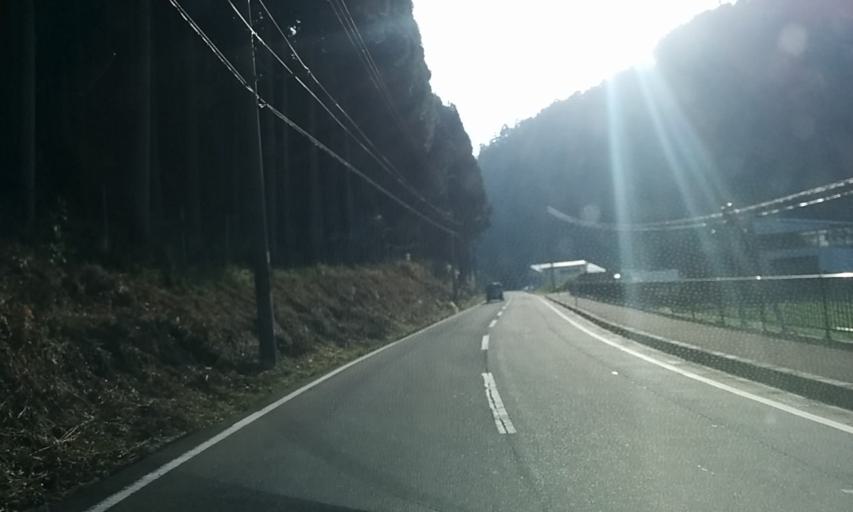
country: JP
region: Fukui
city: Obama
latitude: 35.2949
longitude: 135.6023
